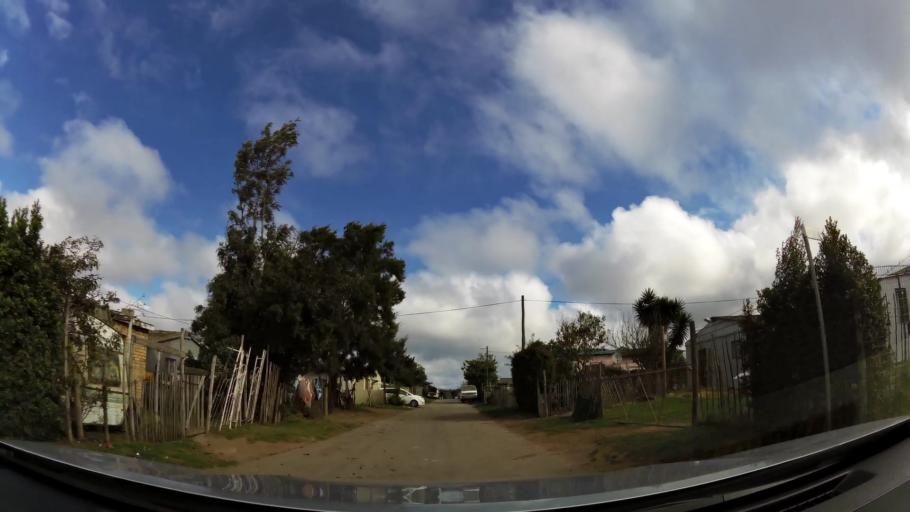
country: ZA
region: Western Cape
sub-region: Eden District Municipality
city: Plettenberg Bay
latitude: -34.0487
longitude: 23.3269
